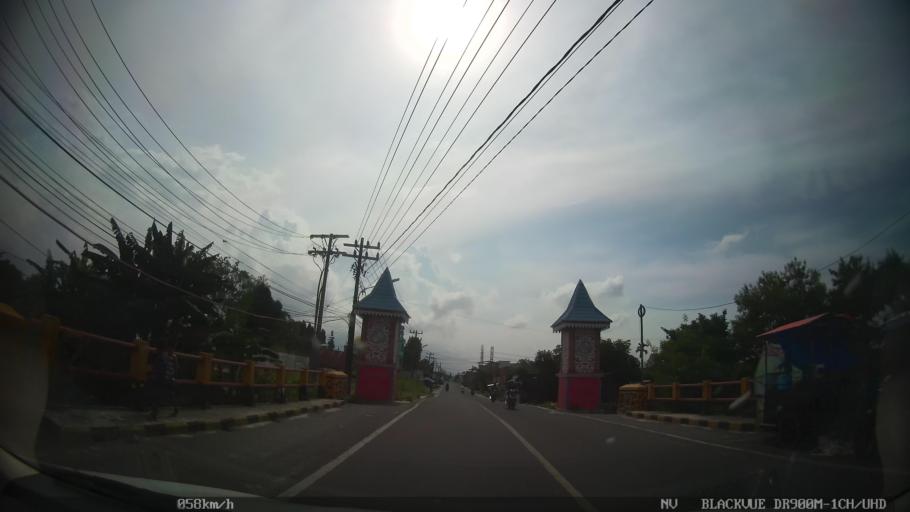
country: ID
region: North Sumatra
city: Percut
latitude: 3.6073
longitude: 98.7922
